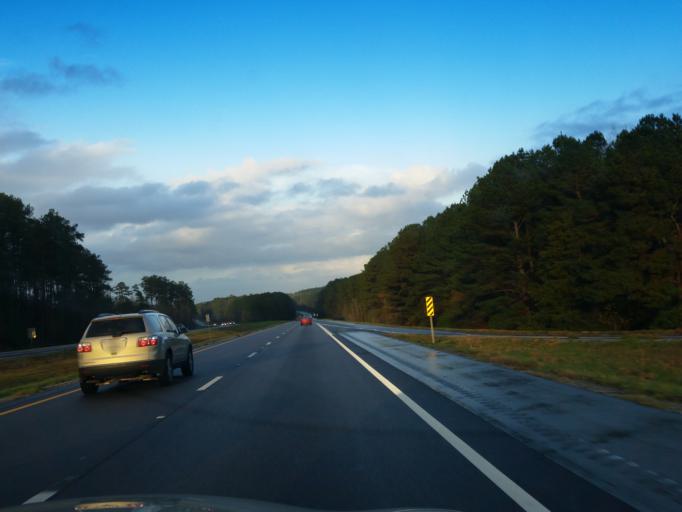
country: US
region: Mississippi
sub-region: Jones County
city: Sharon
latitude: 31.9659
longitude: -88.9657
